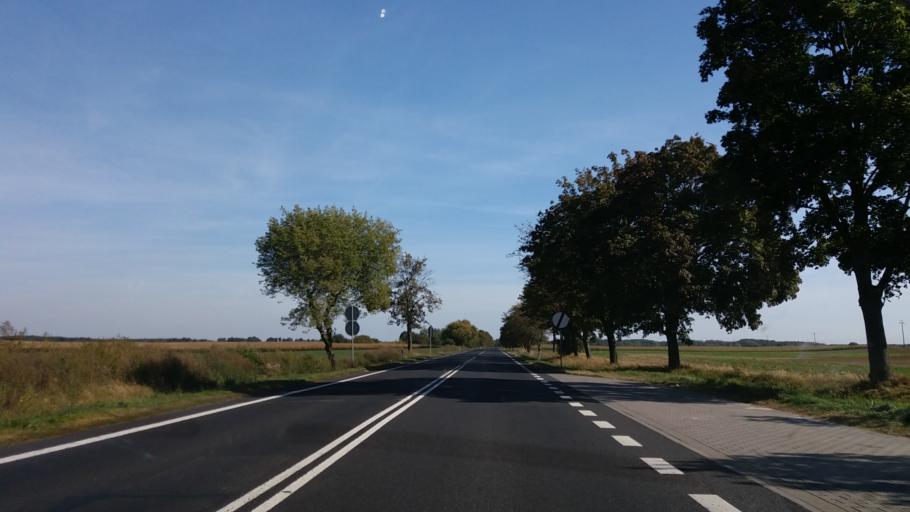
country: PL
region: Greater Poland Voivodeship
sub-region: Powiat miedzychodzki
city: Kwilcz
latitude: 52.5638
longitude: 16.0341
